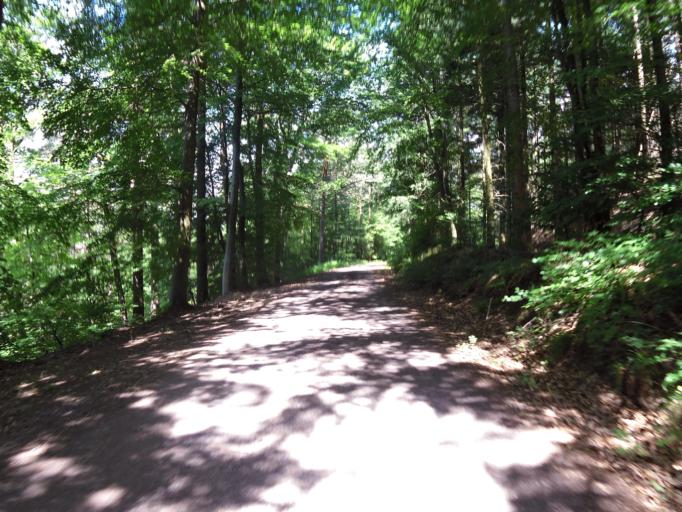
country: DE
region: Rheinland-Pfalz
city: Eusserthal
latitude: 49.2949
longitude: 7.9599
